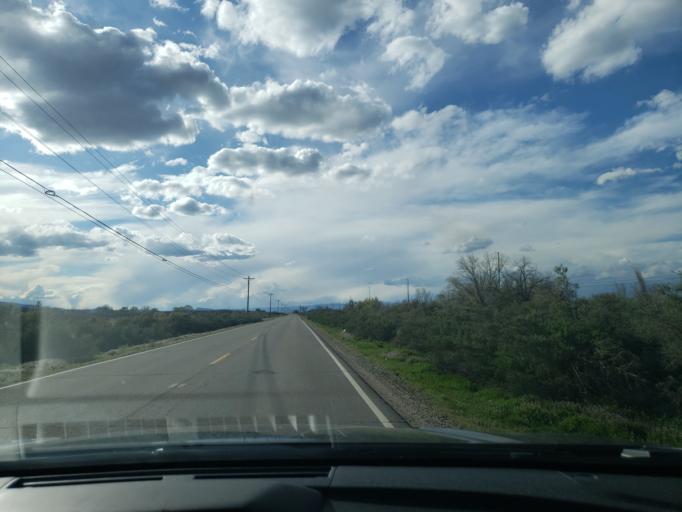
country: US
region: Colorado
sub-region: Mesa County
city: Redlands
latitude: 39.1255
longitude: -108.6763
